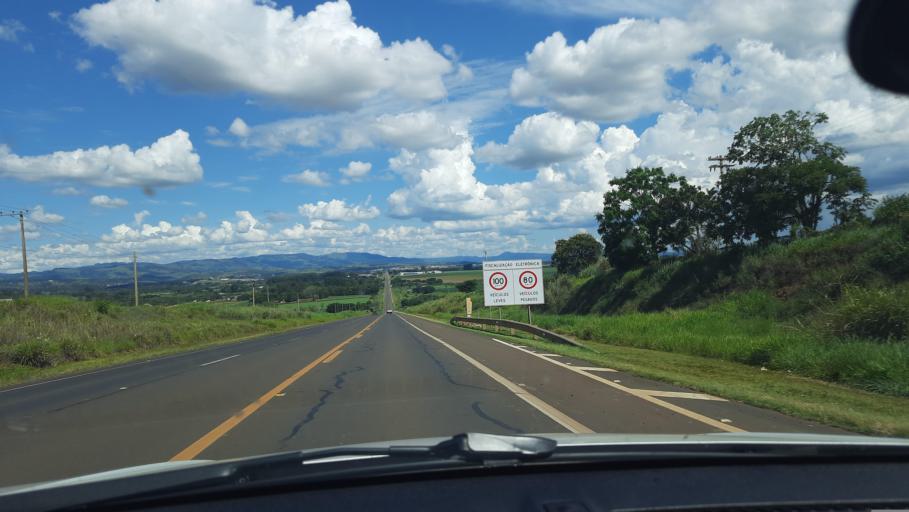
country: BR
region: Sao Paulo
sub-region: Vargem Grande Do Sul
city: Vargem Grande do Sul
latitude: -21.8190
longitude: -46.9705
